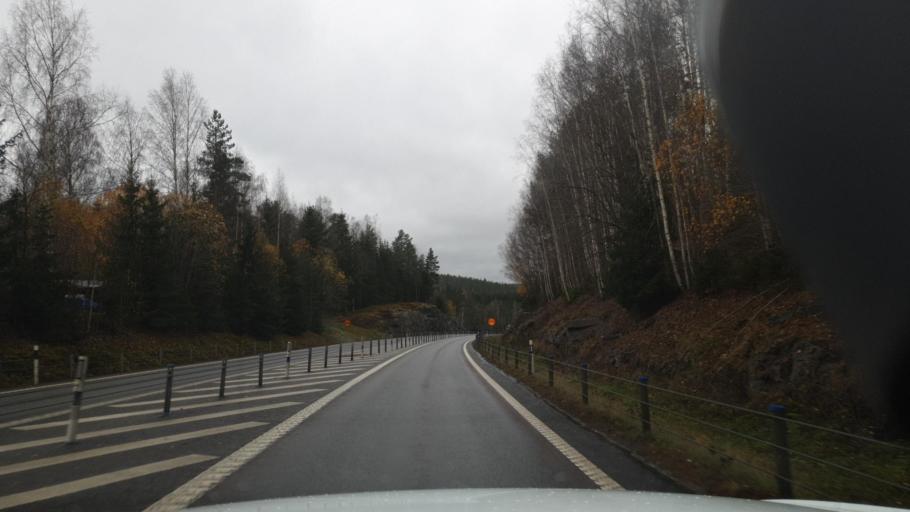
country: SE
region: Vaermland
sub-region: Arvika Kommun
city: Arvika
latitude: 59.6474
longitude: 12.7468
